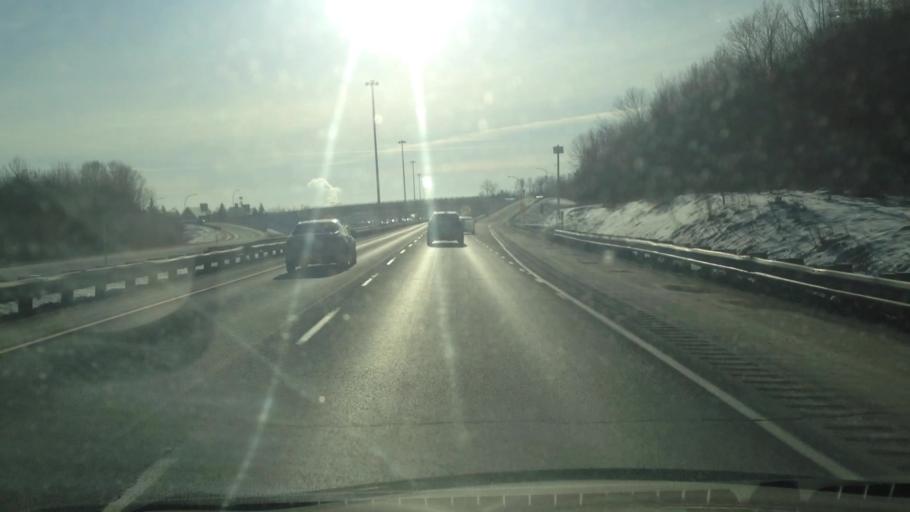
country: CA
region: Quebec
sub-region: Laurentides
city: Prevost
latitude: 45.8454
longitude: -74.0717
